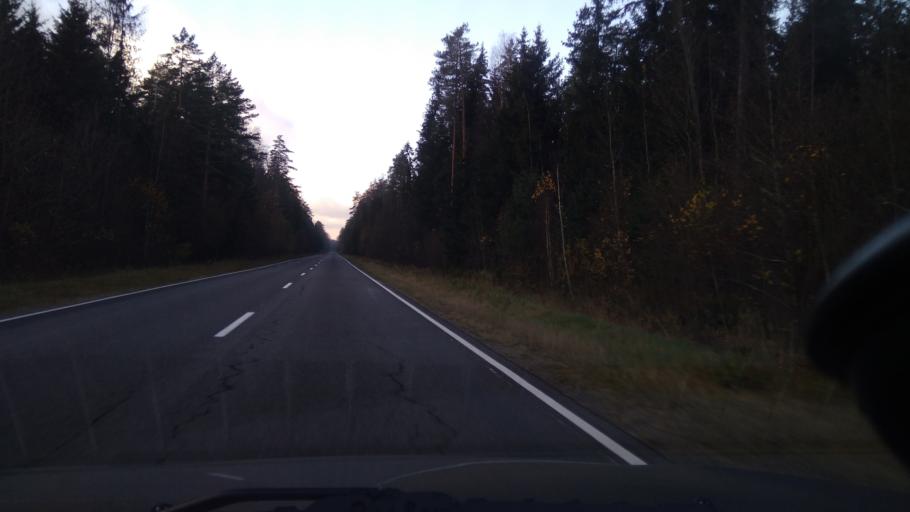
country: BY
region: Minsk
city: Urechcha
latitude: 53.2132
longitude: 27.8731
